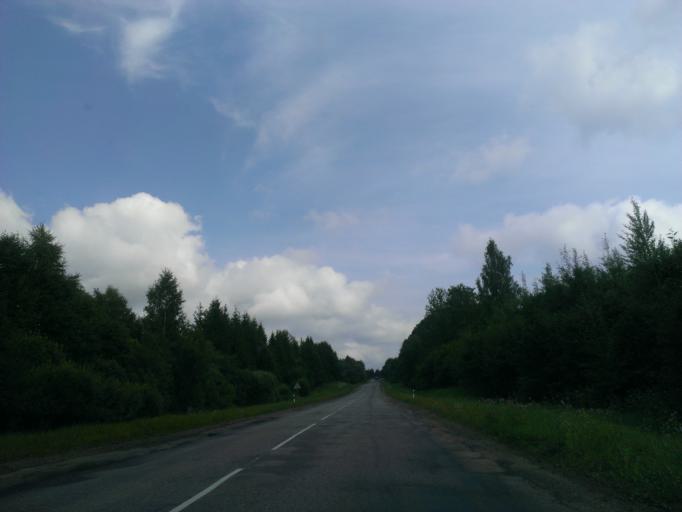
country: LV
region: Priekuli
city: Priekuli
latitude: 57.2705
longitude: 25.4528
